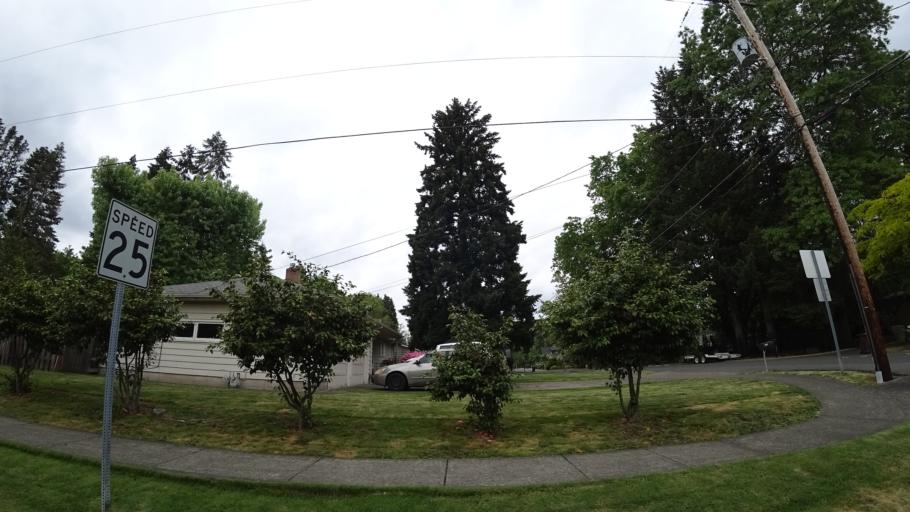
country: US
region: Oregon
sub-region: Washington County
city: Cedar Hills
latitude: 45.4949
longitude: -122.7896
